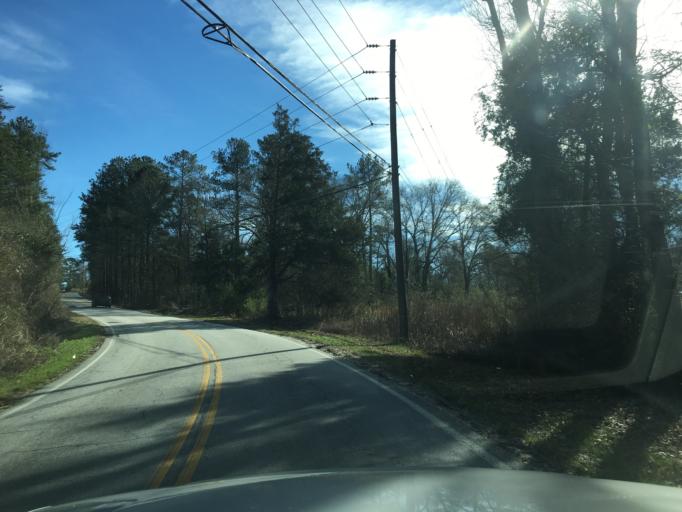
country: US
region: Georgia
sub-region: Rockdale County
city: Lakeview Estates
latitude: 33.7577
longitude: -84.0478
